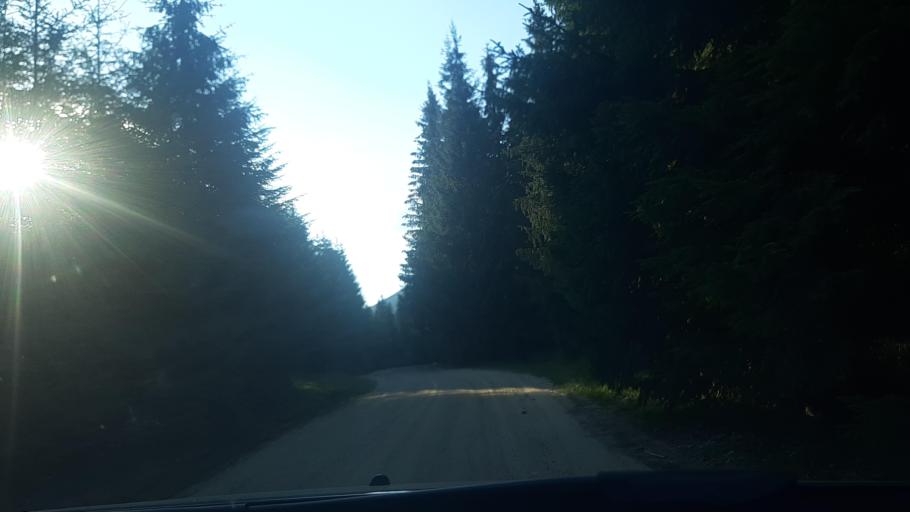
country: RO
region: Alba
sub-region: Comuna Sugag
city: Sugag
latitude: 45.5744
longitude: 23.6111
